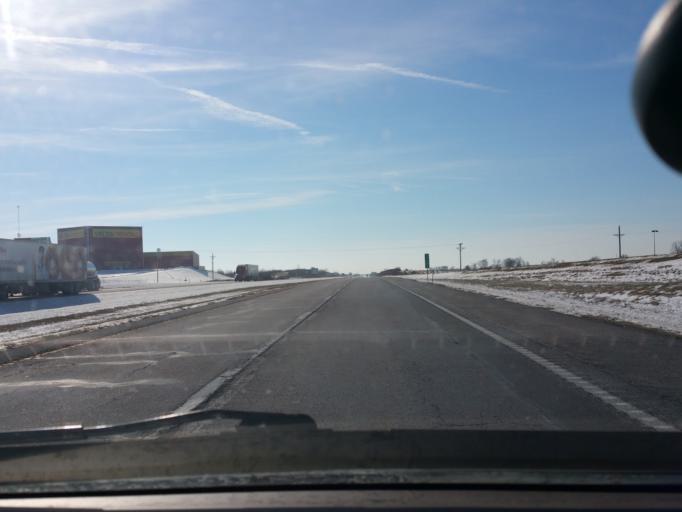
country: US
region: Iowa
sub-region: Decatur County
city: Lamoni
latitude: 40.4658
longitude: -93.9773
